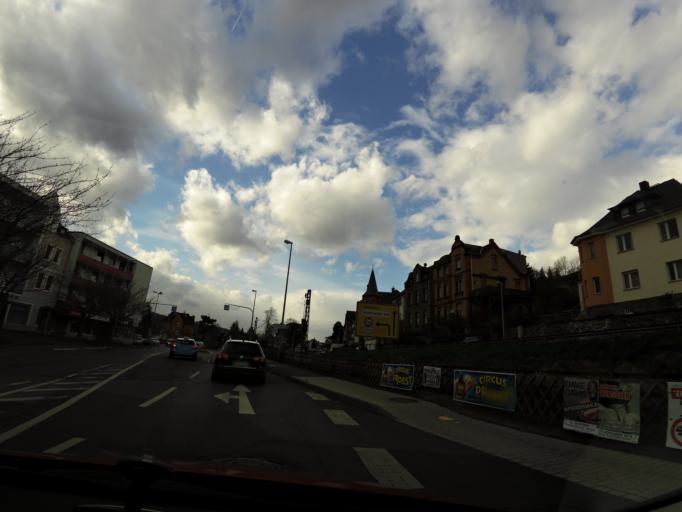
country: DE
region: Rheinland-Pfalz
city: Lahnstein
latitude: 50.3127
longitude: 7.6042
